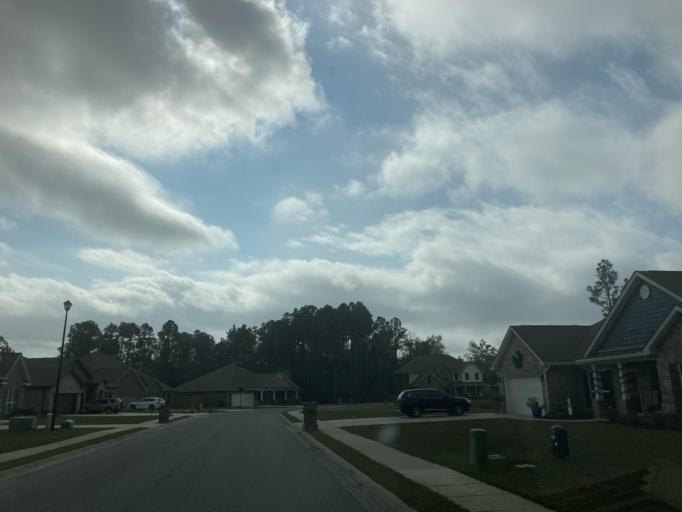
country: US
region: Mississippi
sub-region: Harrison County
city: D'Iberville
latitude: 30.4772
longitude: -88.9812
